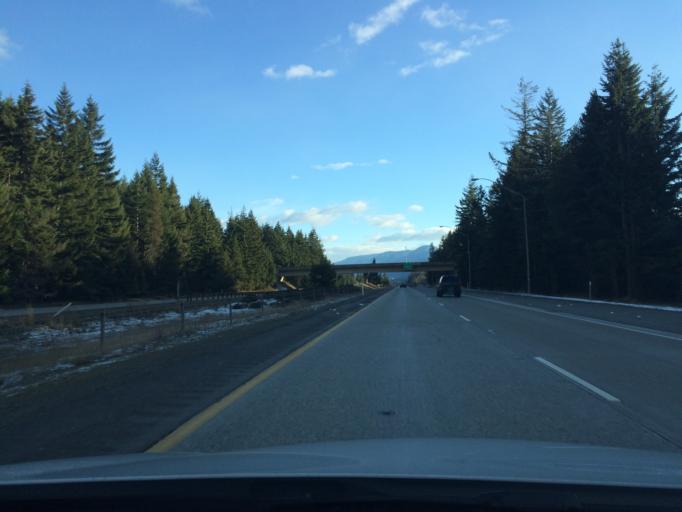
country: US
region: Washington
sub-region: Kittitas County
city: Cle Elum
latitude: 47.2516
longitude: -121.1918
